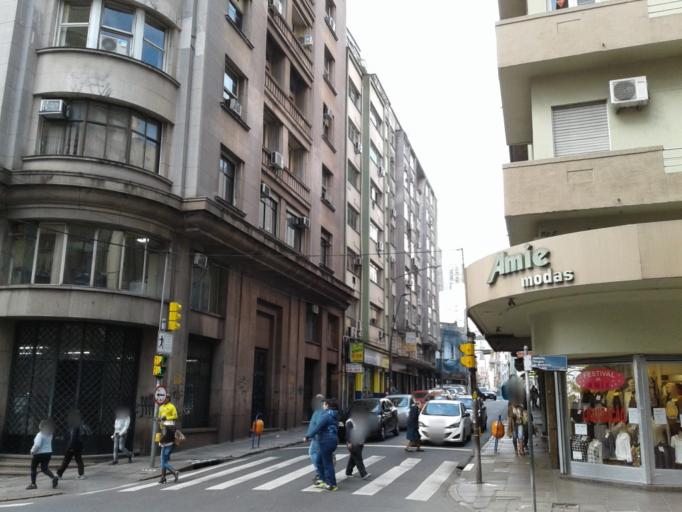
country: BR
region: Rio Grande do Sul
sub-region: Porto Alegre
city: Porto Alegre
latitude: -30.0316
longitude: -51.2278
